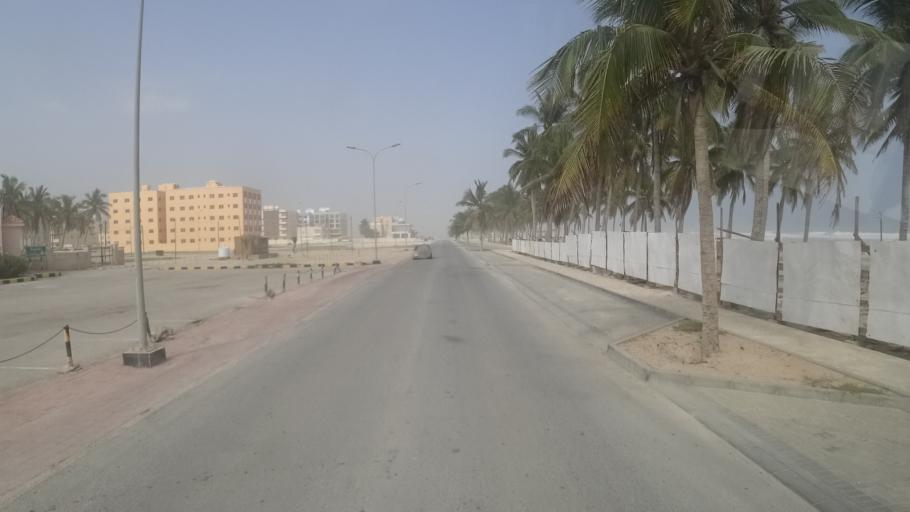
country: OM
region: Zufar
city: Salalah
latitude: 17.0111
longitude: 54.1718
